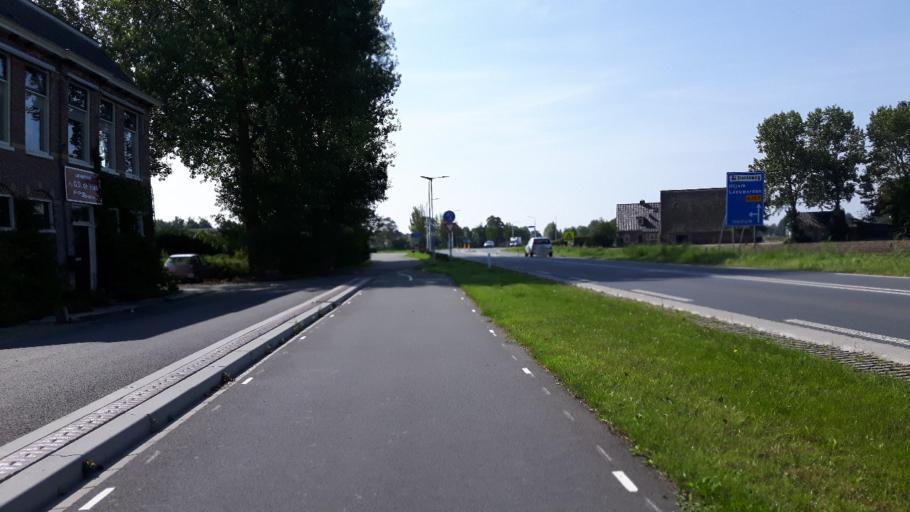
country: NL
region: Friesland
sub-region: Gemeente Ferwerderadiel
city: Hallum
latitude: 53.3115
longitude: 5.7864
